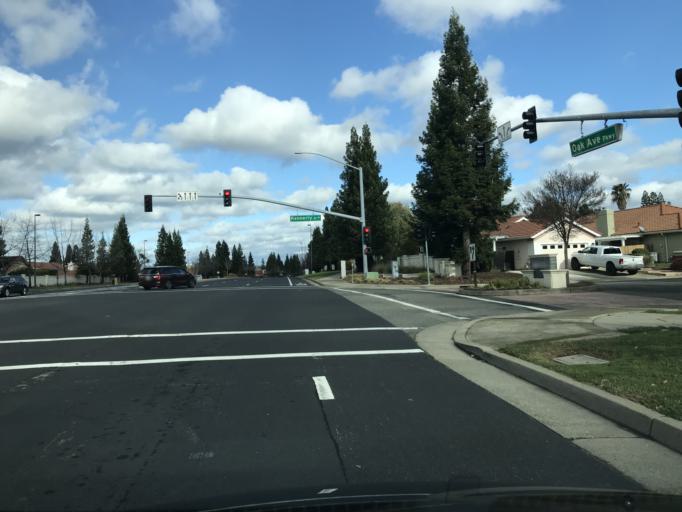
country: US
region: California
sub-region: Sacramento County
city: Folsom
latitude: 38.6589
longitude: -121.1392
